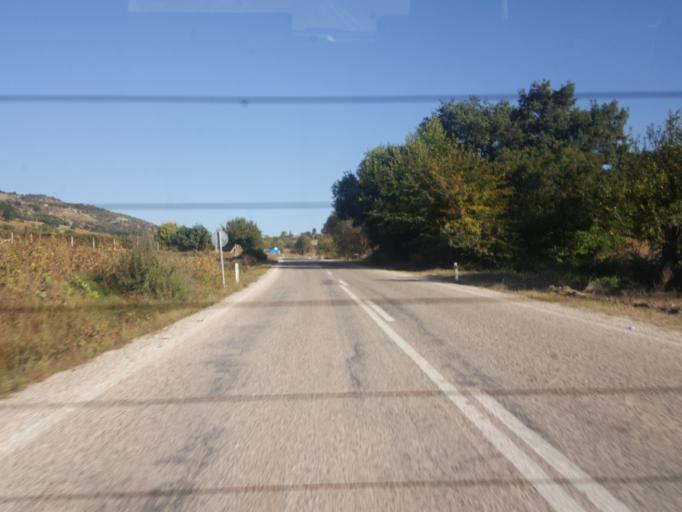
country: TR
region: Amasya
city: Tasova
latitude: 40.7184
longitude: 36.3067
